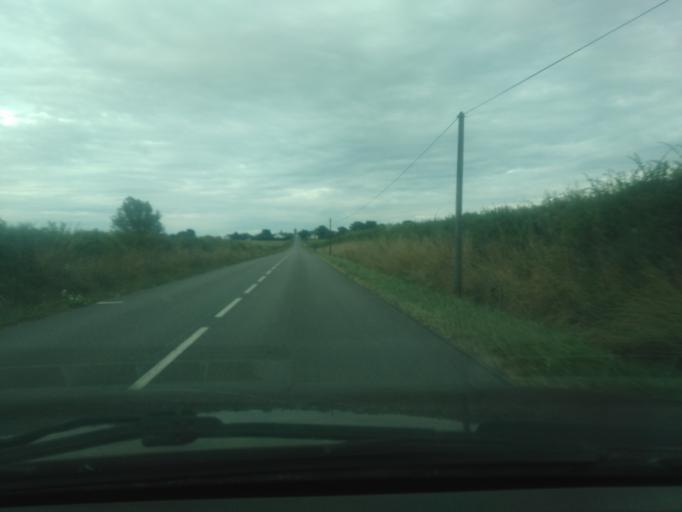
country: FR
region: Bourgogne
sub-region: Departement de la Nievre
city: Dornes
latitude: 46.7765
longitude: 3.3809
